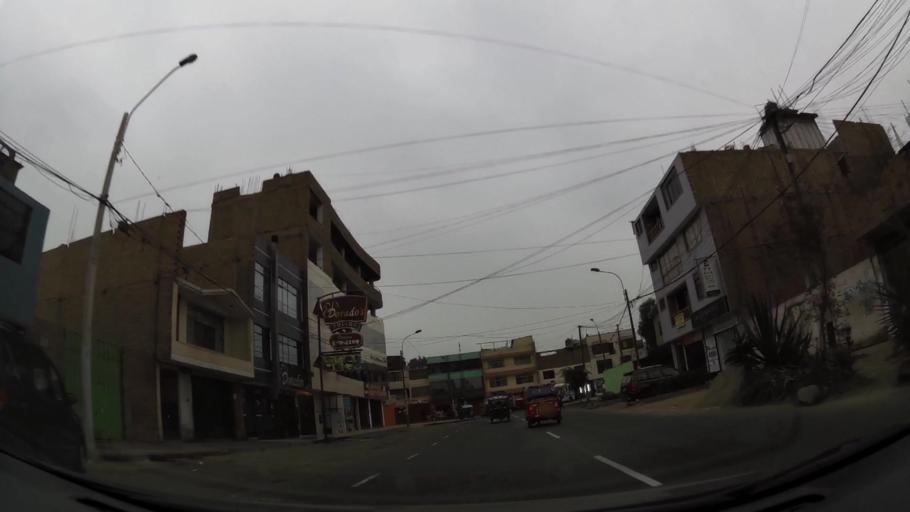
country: PE
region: Lima
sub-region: Lima
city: Independencia
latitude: -11.9341
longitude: -77.0746
